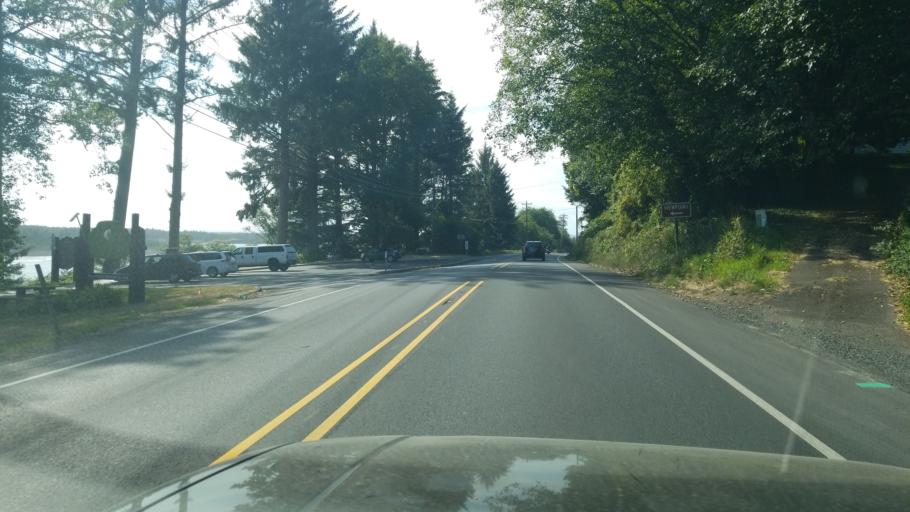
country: US
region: Oregon
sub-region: Tillamook County
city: Bay City
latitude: 45.5592
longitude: -123.9273
